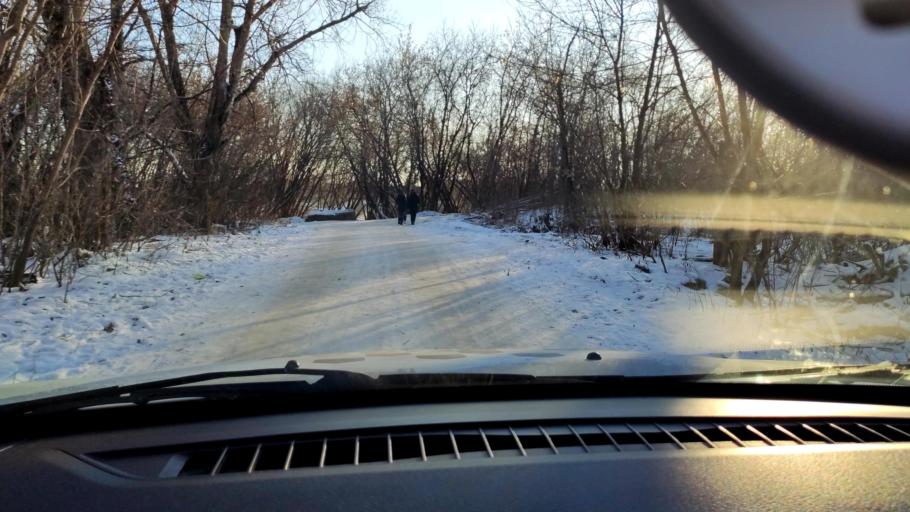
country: RU
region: Perm
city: Kondratovo
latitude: 58.0296
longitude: 56.0309
